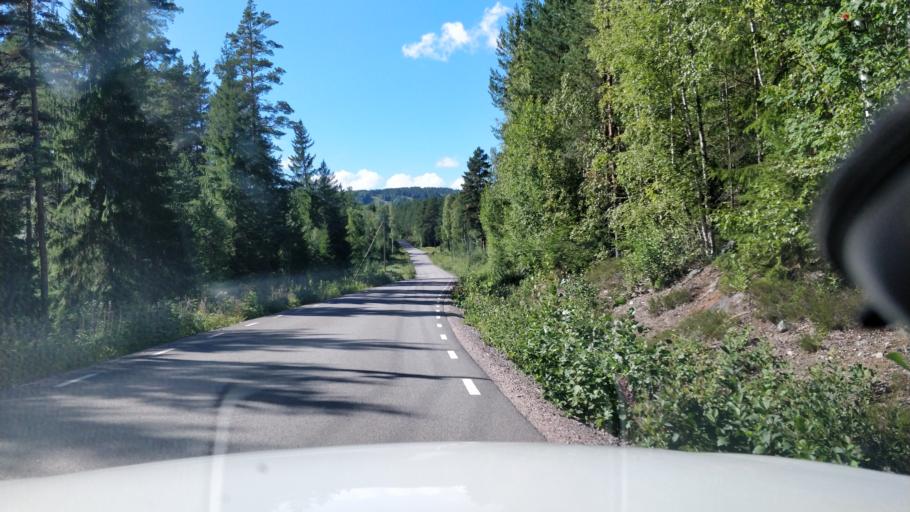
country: SE
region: Dalarna
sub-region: Faluns Kommun
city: Bjursas
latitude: 60.7513
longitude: 15.4982
